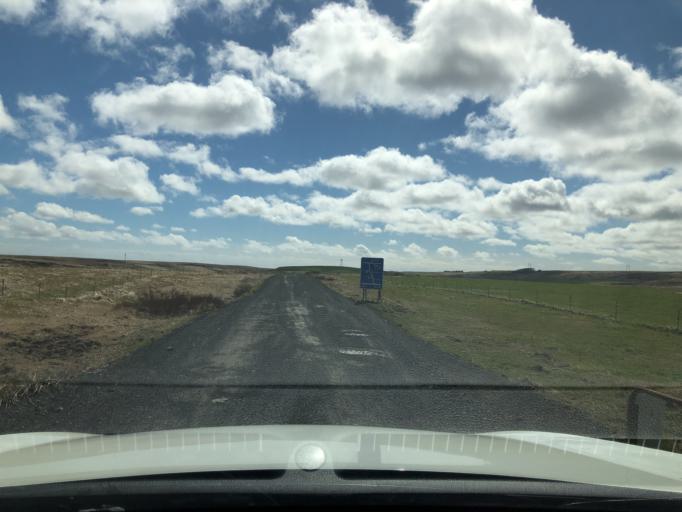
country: IS
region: South
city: Selfoss
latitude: 63.9323
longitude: -20.6688
